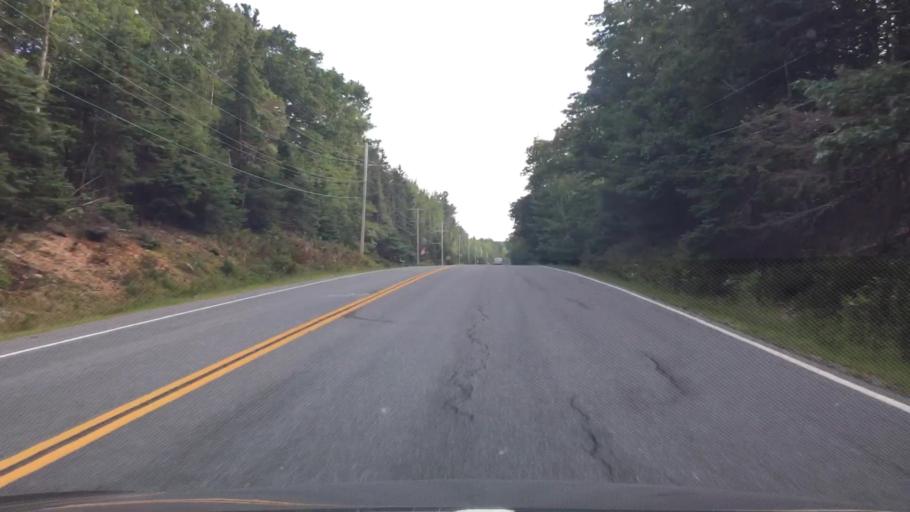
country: US
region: Maine
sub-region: Hancock County
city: Surry
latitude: 44.4890
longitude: -68.5106
